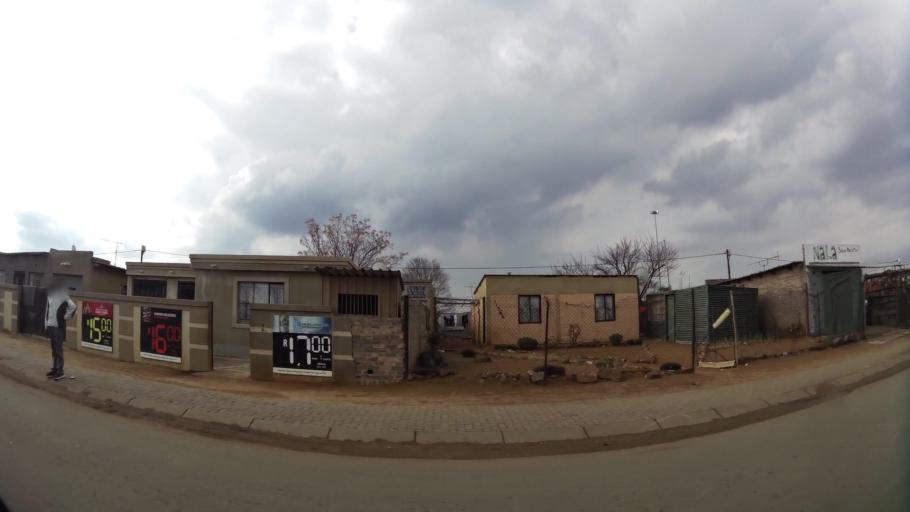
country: ZA
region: Gauteng
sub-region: Sedibeng District Municipality
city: Vanderbijlpark
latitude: -26.7017
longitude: 27.8036
